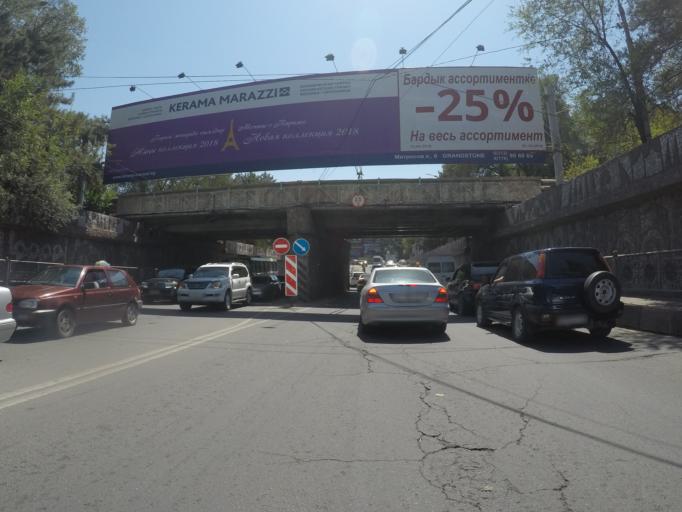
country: KG
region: Chuy
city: Bishkek
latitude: 42.8676
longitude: 74.5748
